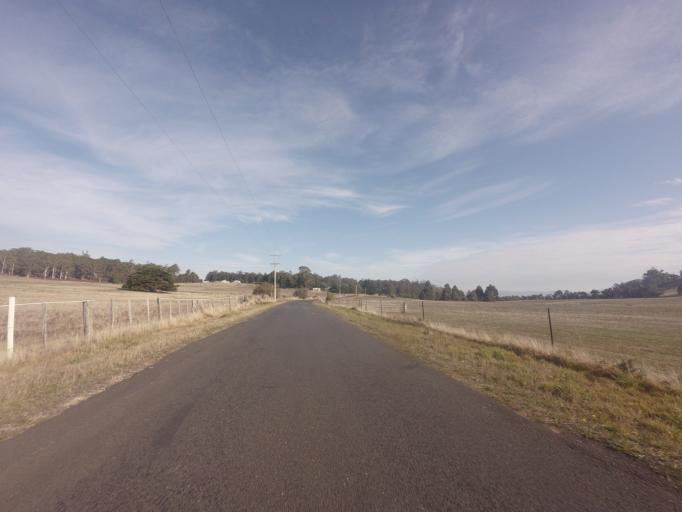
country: AU
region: Tasmania
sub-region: Sorell
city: Sorell
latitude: -42.4792
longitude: 147.4572
